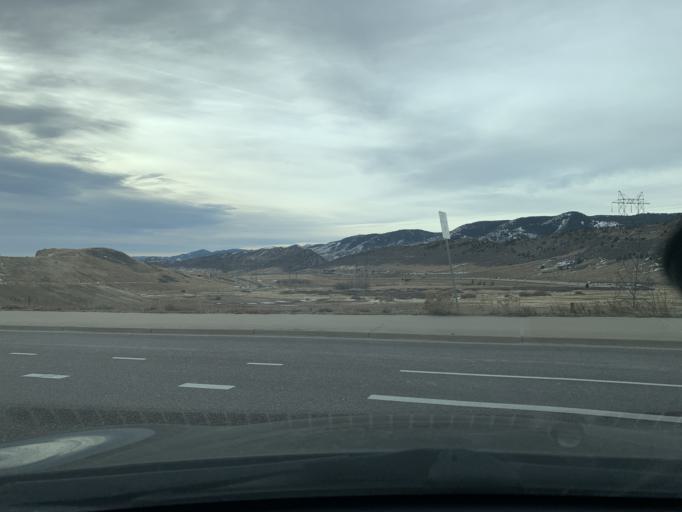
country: US
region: Colorado
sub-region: Jefferson County
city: West Pleasant View
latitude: 39.6851
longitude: -105.1842
